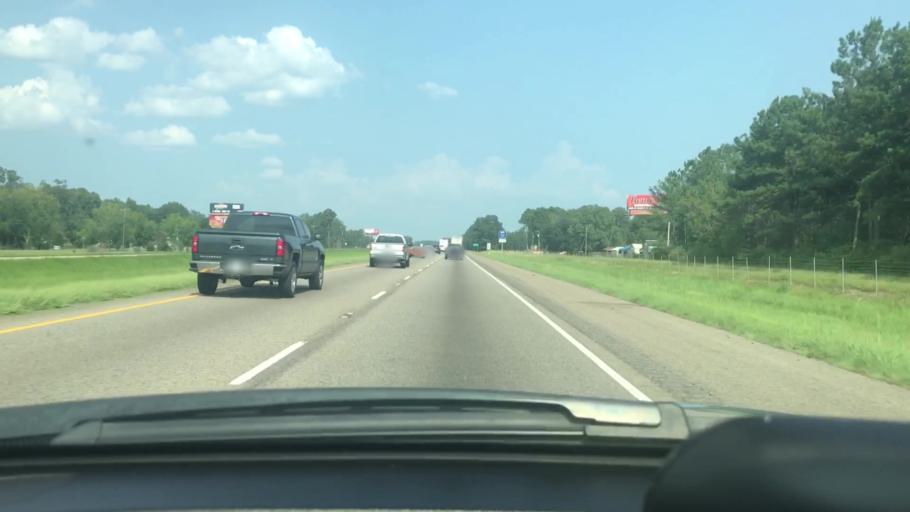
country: US
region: Louisiana
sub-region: Livingston Parish
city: Albany
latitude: 30.4747
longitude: -90.6327
